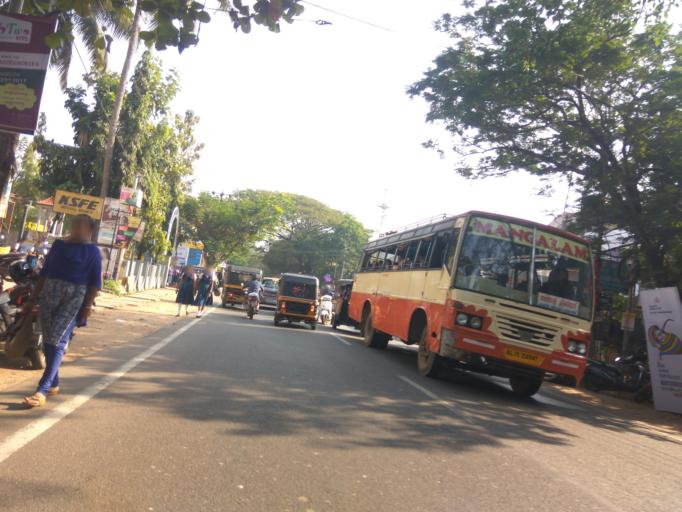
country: IN
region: Kerala
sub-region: Kozhikode
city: Kozhikode
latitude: 11.2854
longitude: 75.7683
